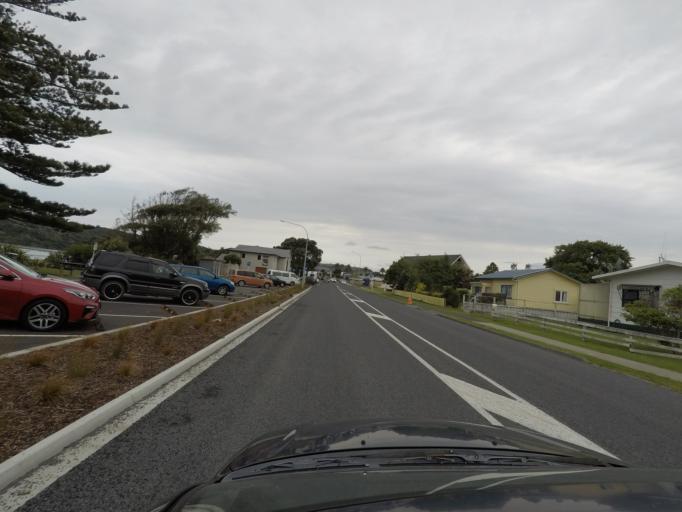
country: NZ
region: Waikato
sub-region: Waikato District
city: Raglan
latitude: -37.8028
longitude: 174.8685
